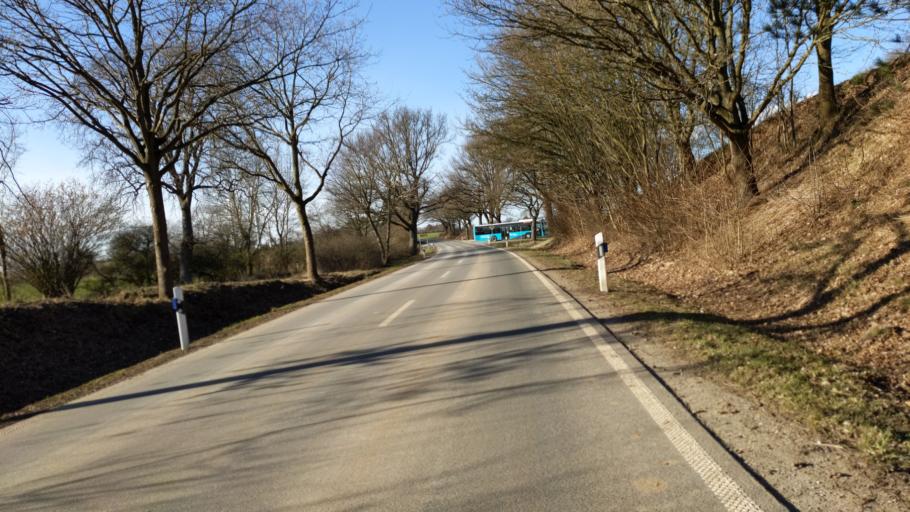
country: DE
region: Schleswig-Holstein
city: Susel
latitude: 54.0631
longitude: 10.6467
